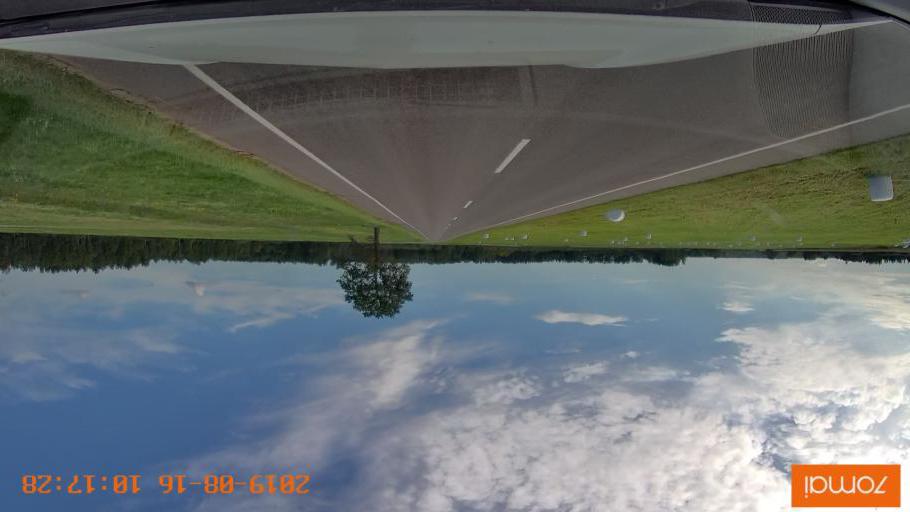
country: BY
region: Mogilev
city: Asipovichy
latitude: 53.3104
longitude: 28.7108
